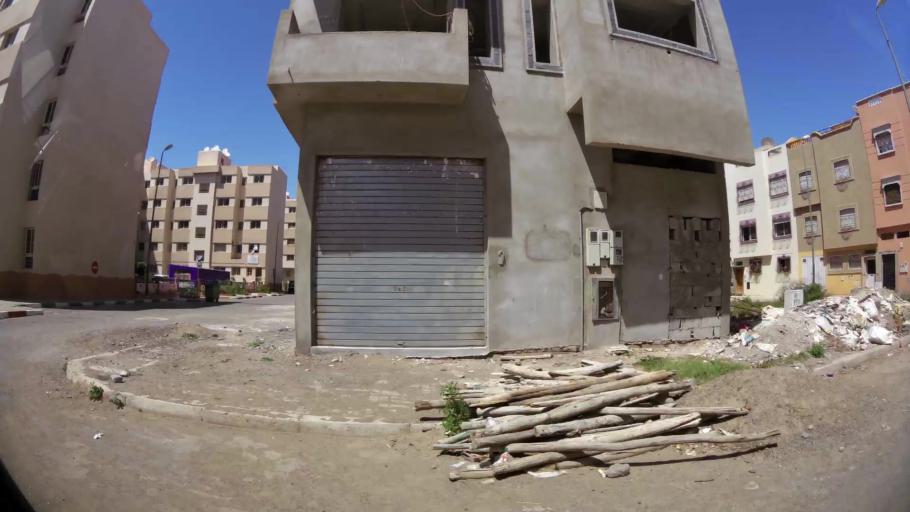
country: MA
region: Souss-Massa-Draa
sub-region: Inezgane-Ait Mellou
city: Inezgane
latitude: 30.3422
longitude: -9.5161
